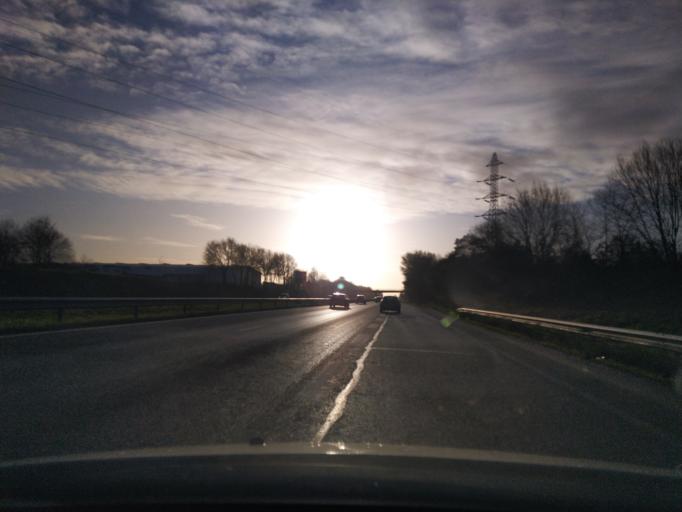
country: FR
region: Haute-Normandie
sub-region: Departement de la Seine-Maritime
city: Maromme
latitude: 49.4803
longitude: 1.0115
